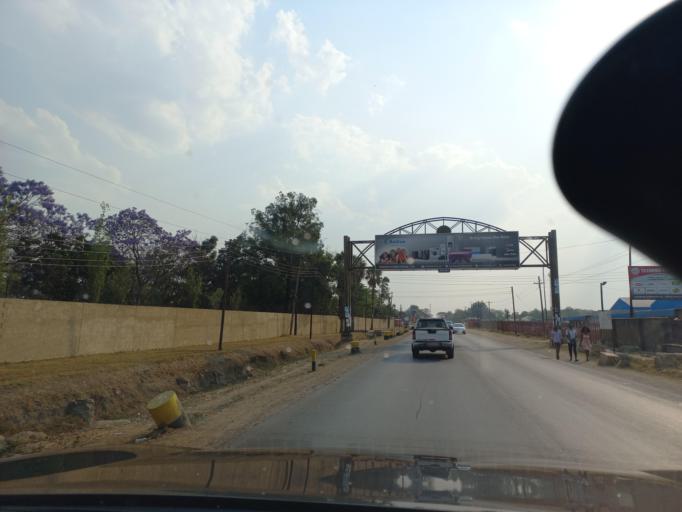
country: ZM
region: Lusaka
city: Lusaka
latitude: -15.4572
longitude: 28.2607
